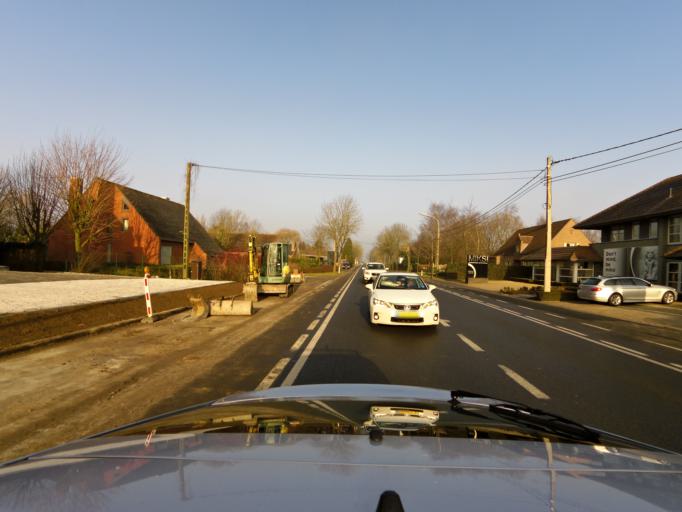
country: BE
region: Flanders
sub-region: Provincie West-Vlaanderen
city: Ichtegem
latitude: 51.1218
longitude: 2.9989
